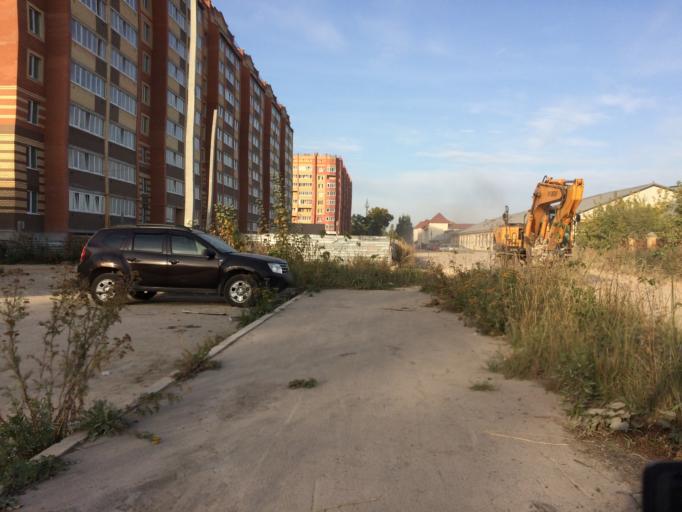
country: RU
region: Mariy-El
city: Yoshkar-Ola
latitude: 56.6266
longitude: 47.8502
